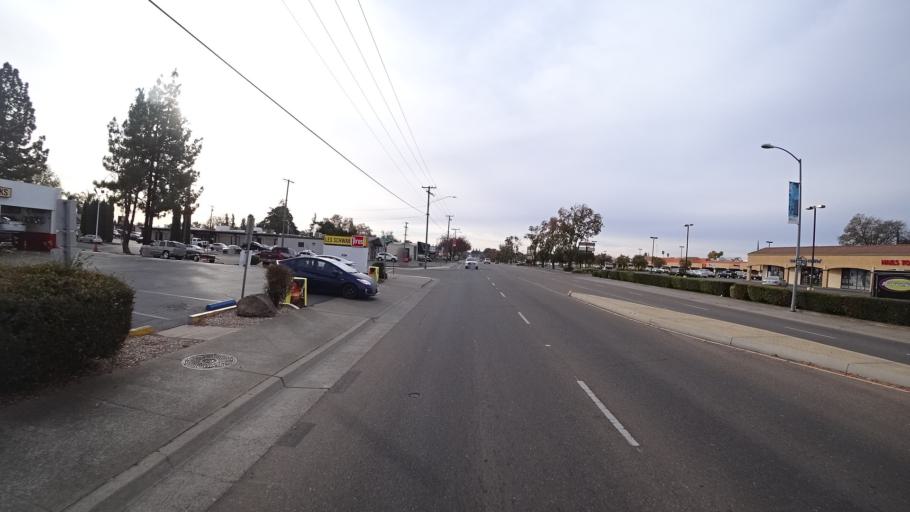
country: US
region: California
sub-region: Sacramento County
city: Citrus Heights
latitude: 38.7137
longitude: -121.2903
